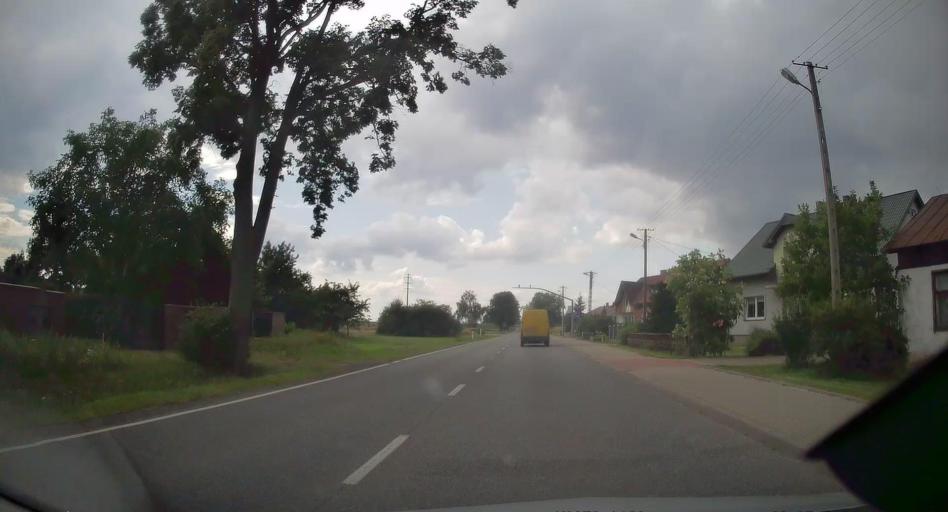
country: PL
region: Lodz Voivodeship
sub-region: Powiat skierniewicki
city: Gluchow
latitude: 51.7752
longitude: 20.1250
